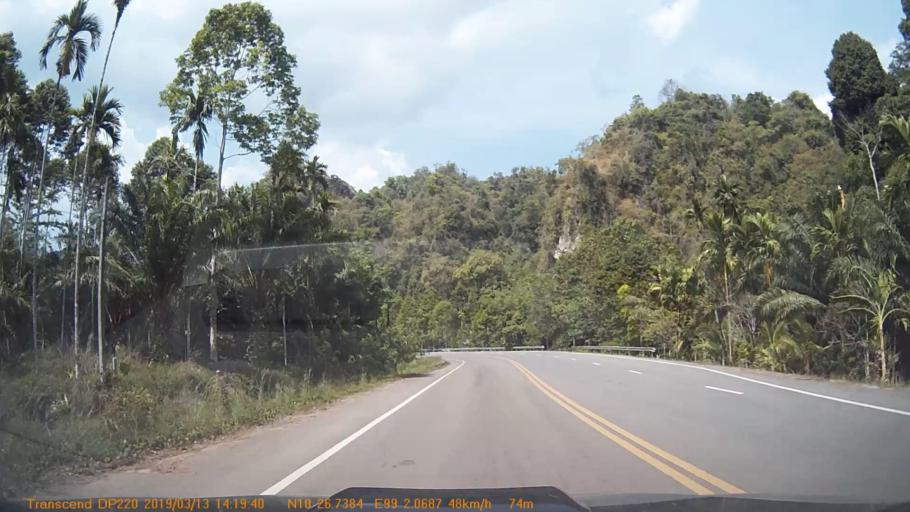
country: TH
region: Chumphon
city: Chumphon
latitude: 10.4459
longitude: 99.0345
